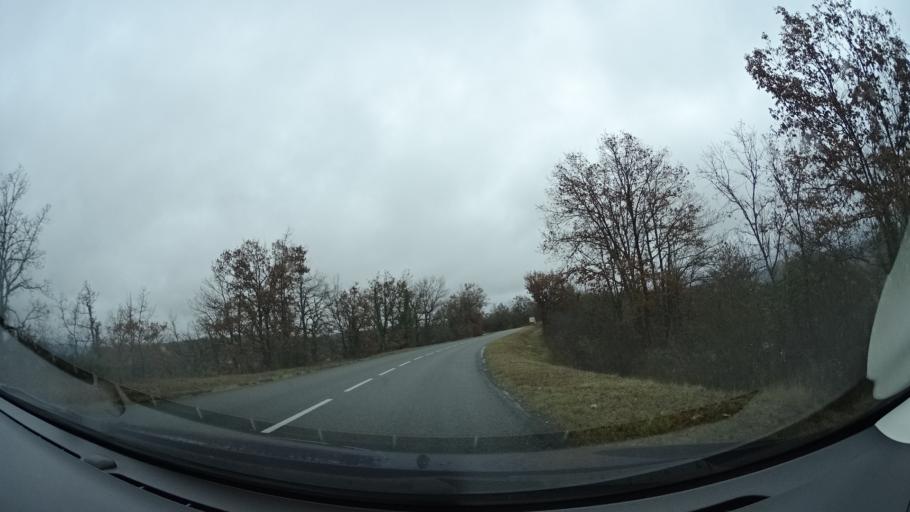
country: FR
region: Midi-Pyrenees
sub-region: Departement du Tarn-et-Garonne
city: Lauzerte
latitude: 44.2332
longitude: 1.1391
